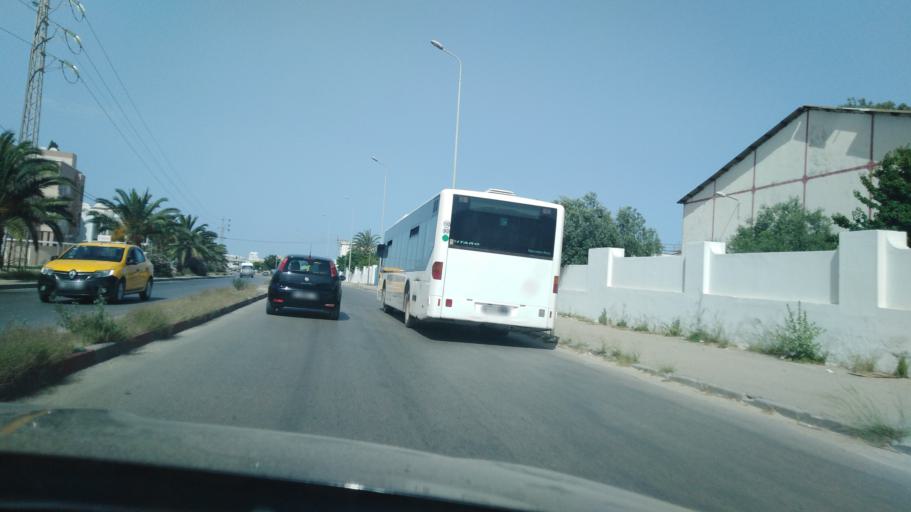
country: TN
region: Susah
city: Sousse
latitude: 35.7998
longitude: 10.6103
